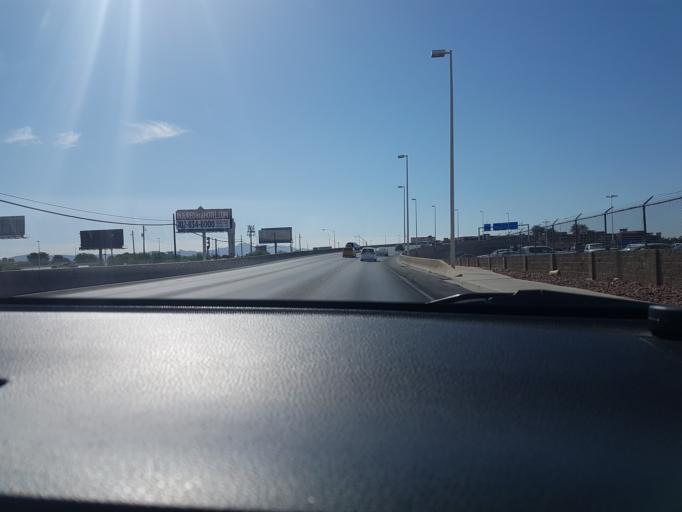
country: US
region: Nevada
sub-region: Clark County
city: Paradise
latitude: 36.0945
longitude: -115.1480
